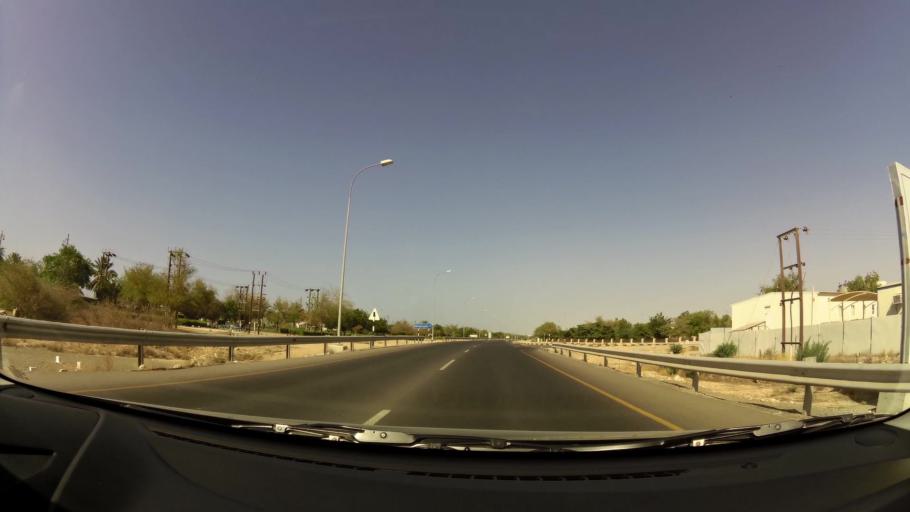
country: OM
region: Muhafazat Masqat
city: Bawshar
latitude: 23.5861
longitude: 58.3020
